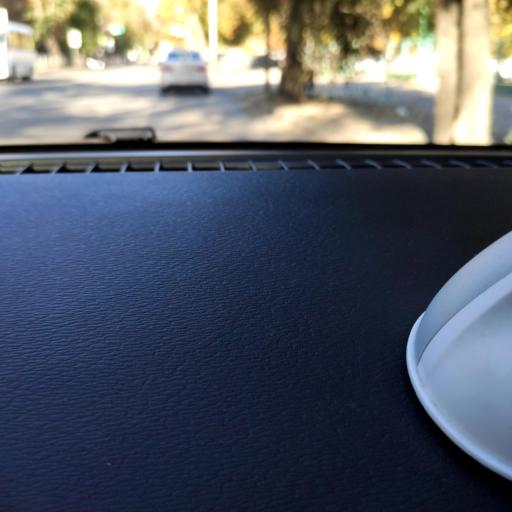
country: RU
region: Samara
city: Samara
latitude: 53.1941
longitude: 50.1387
